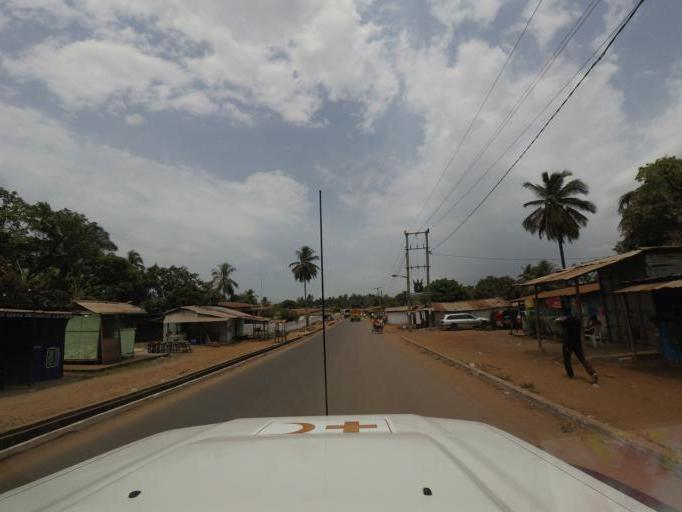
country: LR
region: Montserrado
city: Monrovia
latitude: 6.3024
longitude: -10.7048
